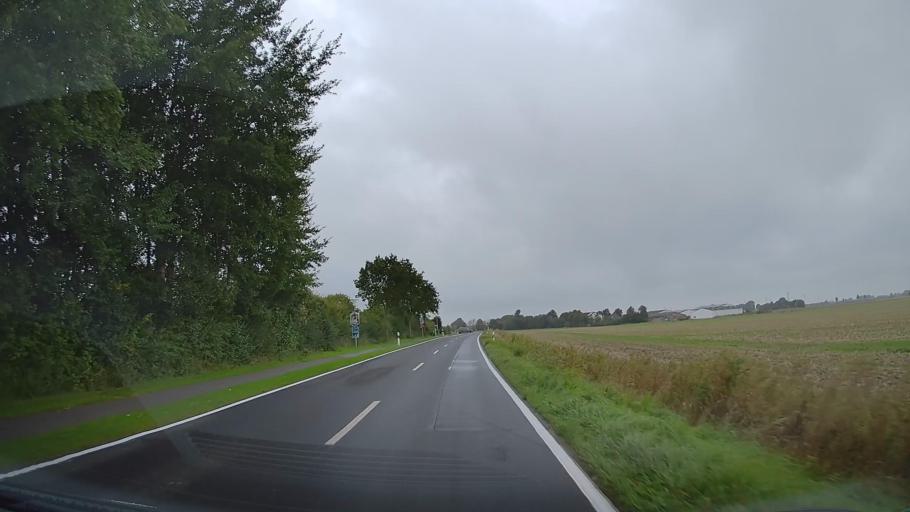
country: DE
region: Schleswig-Holstein
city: Wesselburener Deichhausen
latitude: 54.1423
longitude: 8.9250
